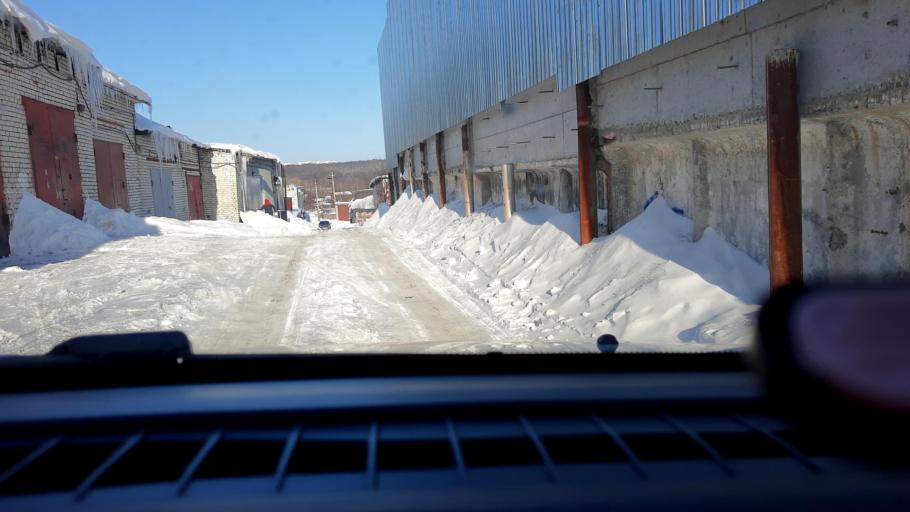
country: RU
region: Nizjnij Novgorod
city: Afonino
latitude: 56.2384
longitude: 44.0095
